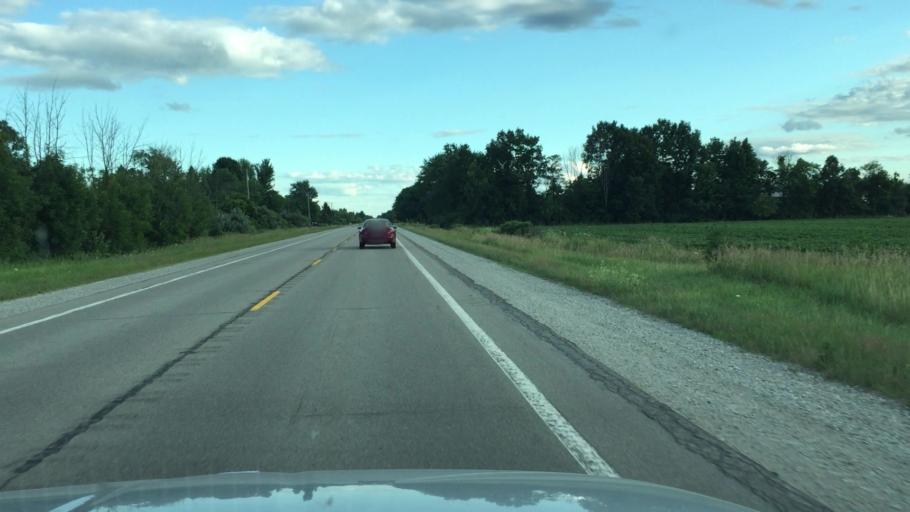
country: US
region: Michigan
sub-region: Saint Clair County
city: Yale
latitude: 43.0422
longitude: -82.7634
